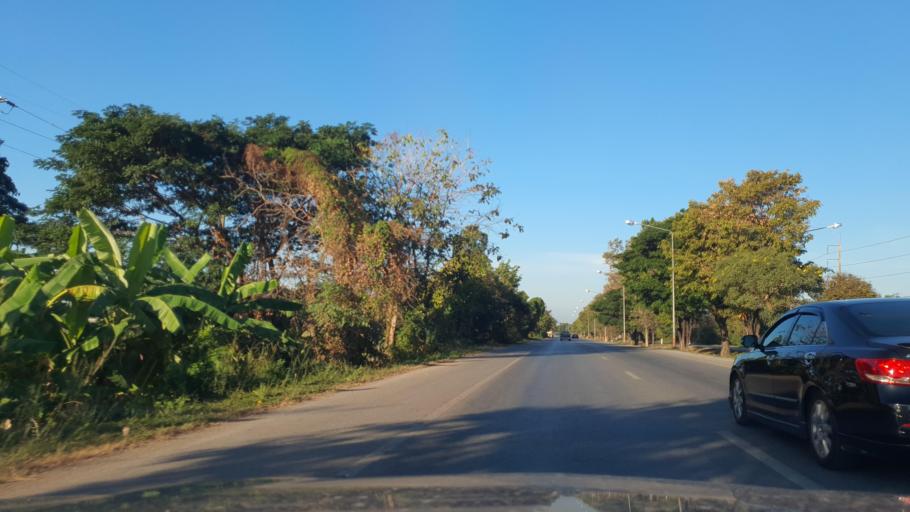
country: TH
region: Phitsanulok
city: Phitsanulok
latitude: 16.8651
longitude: 100.2275
